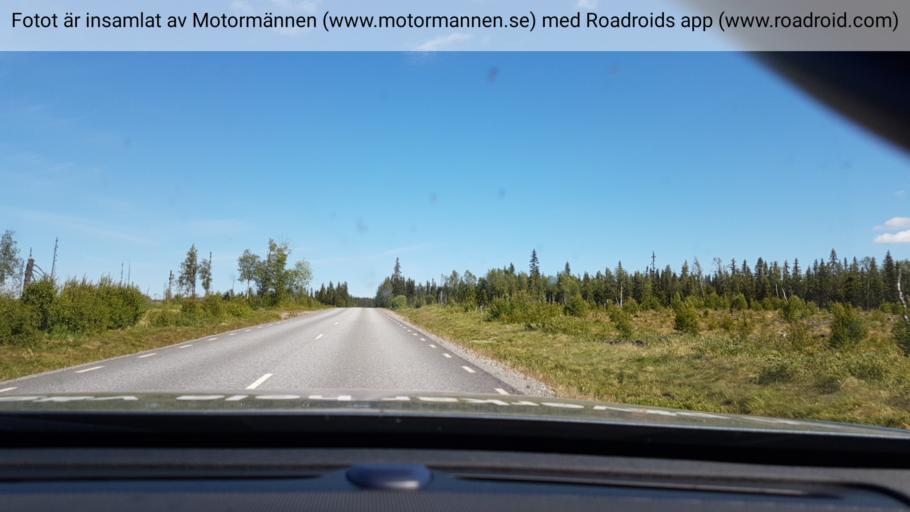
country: SE
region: Vaesterbotten
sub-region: Asele Kommun
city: Insjon
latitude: 64.7039
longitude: 17.2282
